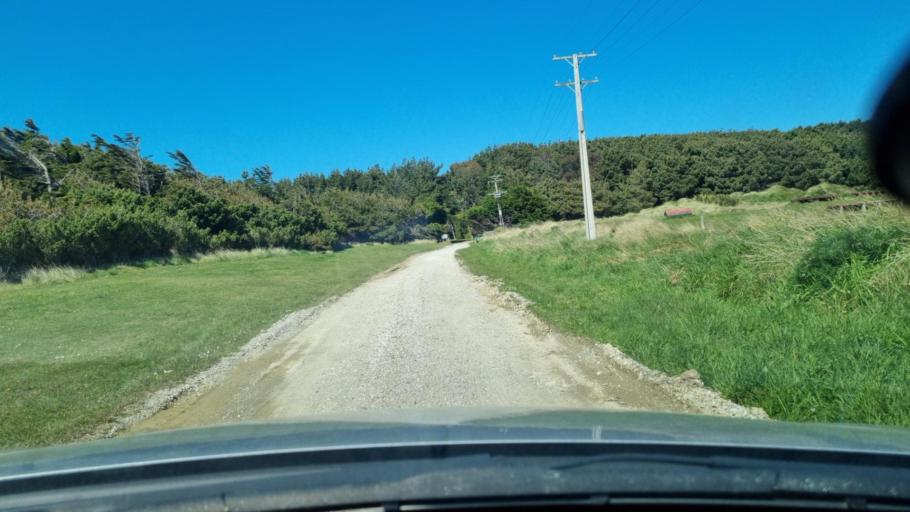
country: NZ
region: Southland
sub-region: Invercargill City
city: Invercargill
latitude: -46.4399
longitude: 168.2396
